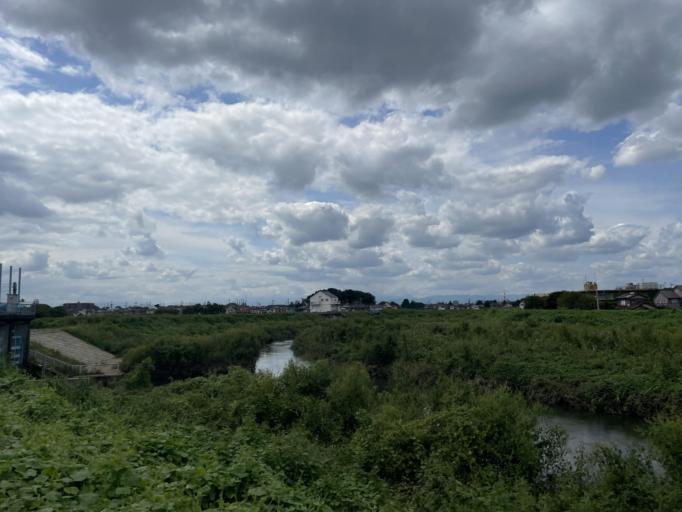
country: JP
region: Saitama
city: Kamifukuoka
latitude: 35.8895
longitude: 139.5173
